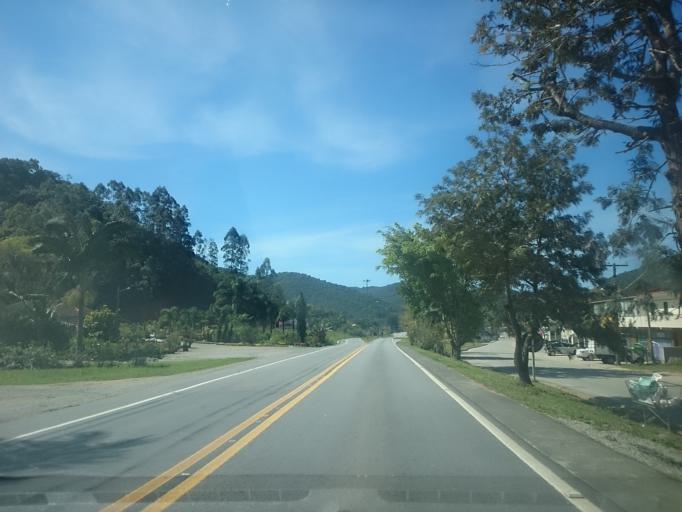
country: BR
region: Santa Catarina
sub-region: Santo Amaro Da Imperatriz
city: Santo Amaro da Imperatriz
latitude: -27.7196
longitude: -48.8849
